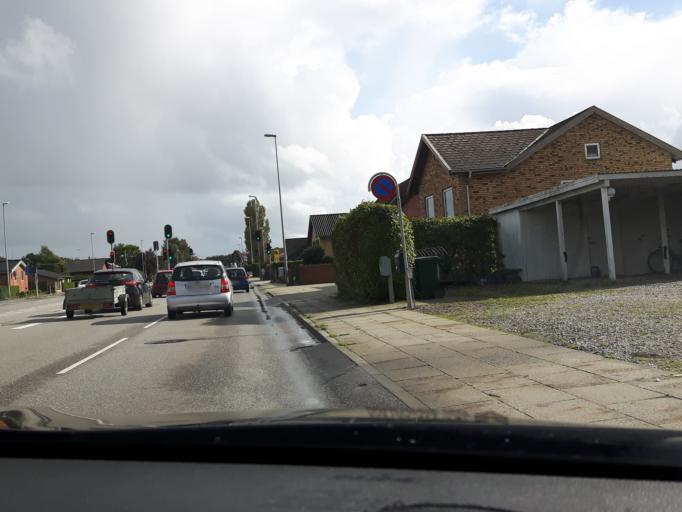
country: DK
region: Central Jutland
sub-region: Herning Kommune
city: Herning
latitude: 56.1406
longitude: 8.9442
